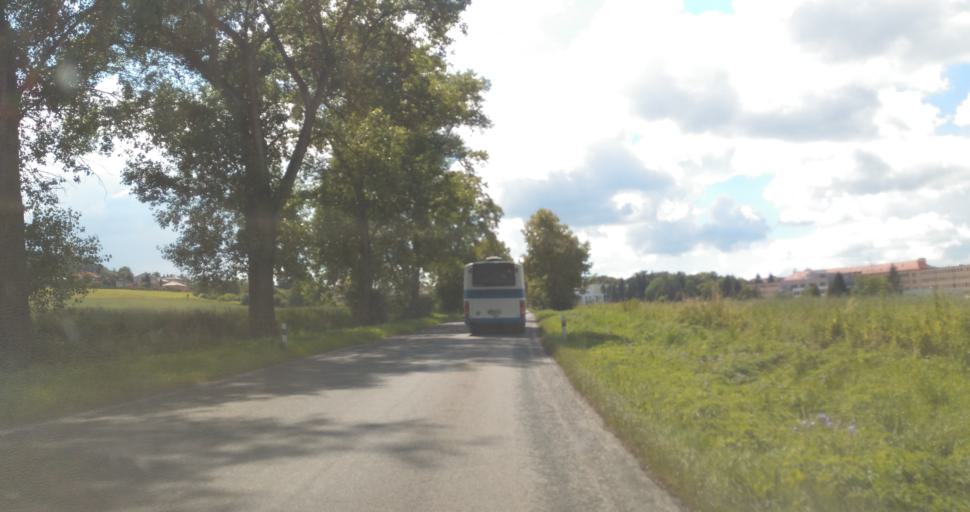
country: CZ
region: Central Bohemia
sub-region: Okres Beroun
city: Horovice
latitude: 49.8396
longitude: 13.9229
